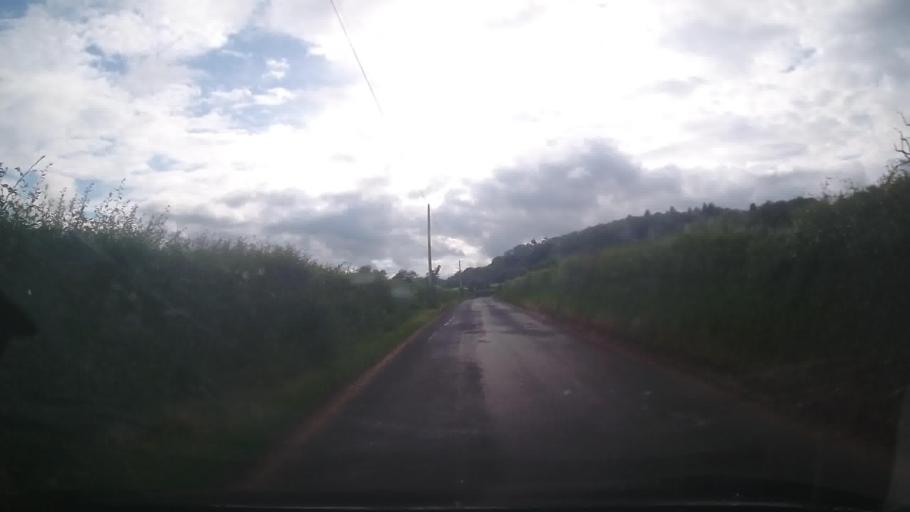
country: GB
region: England
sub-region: Shropshire
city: Prees
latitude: 52.8564
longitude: -2.6167
